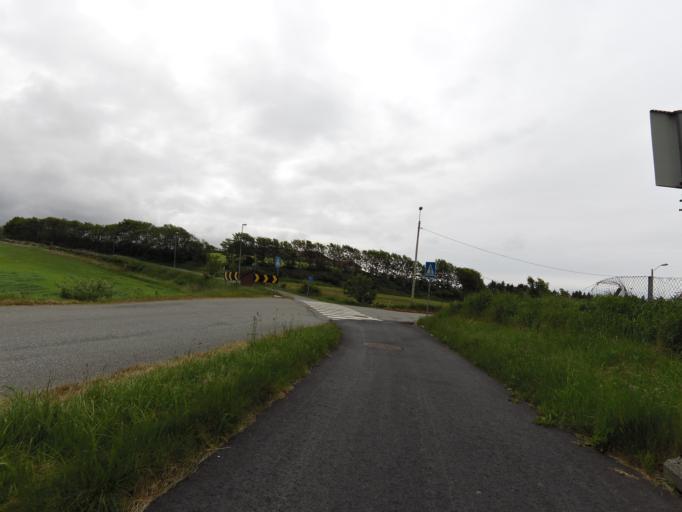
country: NO
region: Rogaland
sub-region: Klepp
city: Kleppe
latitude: 58.8207
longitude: 5.5876
